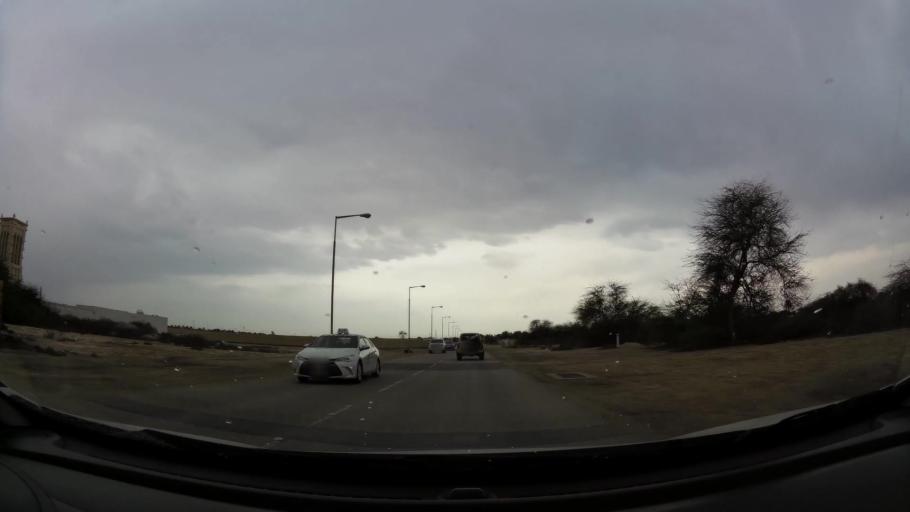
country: BH
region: Central Governorate
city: Madinat Hamad
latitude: 26.1649
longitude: 50.4574
